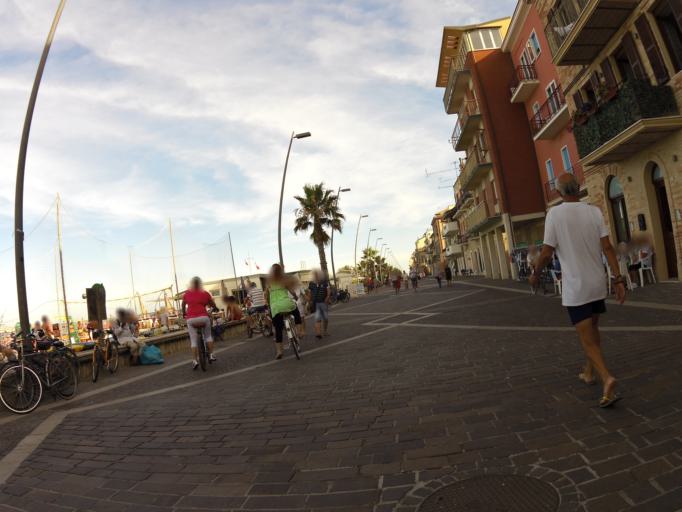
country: IT
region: The Marches
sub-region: Provincia di Macerata
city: Porto Recanati
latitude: 43.4347
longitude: 13.6645
